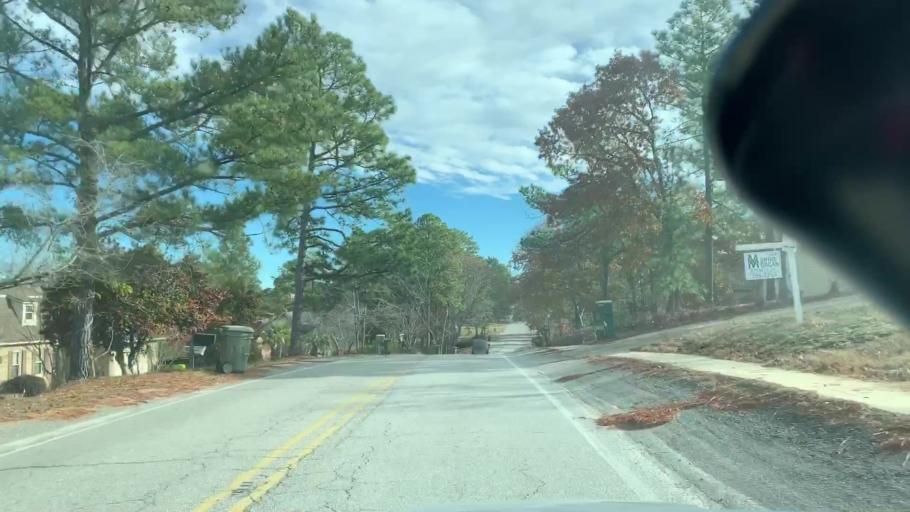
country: US
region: South Carolina
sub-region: Richland County
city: Woodfield
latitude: 34.0638
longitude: -80.9359
